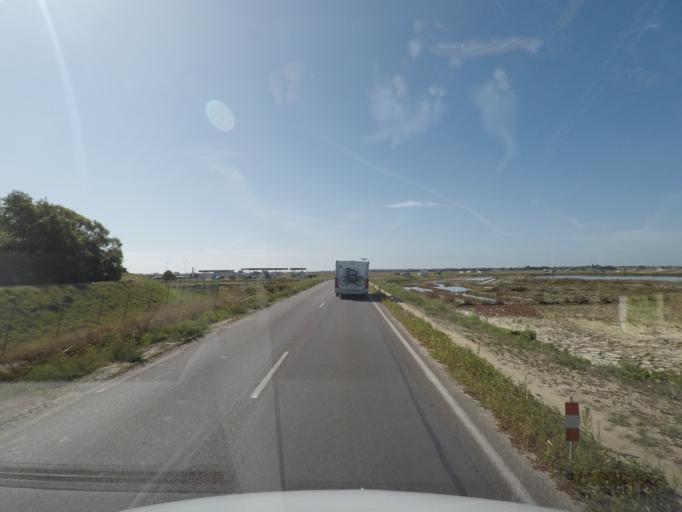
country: FR
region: Pays de la Loire
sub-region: Departement de la Vendee
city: La Gueriniere
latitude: 46.9926
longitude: -2.2500
